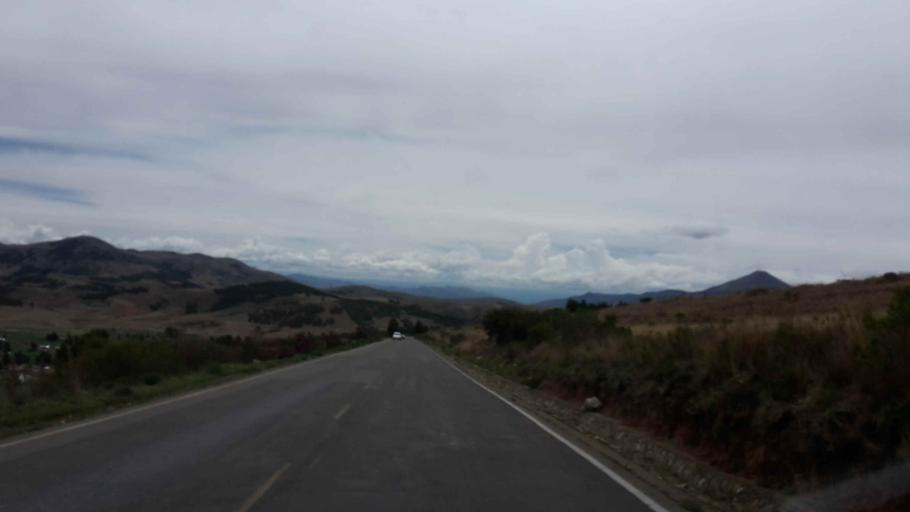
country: BO
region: Cochabamba
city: Arani
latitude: -17.4632
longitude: -65.6886
